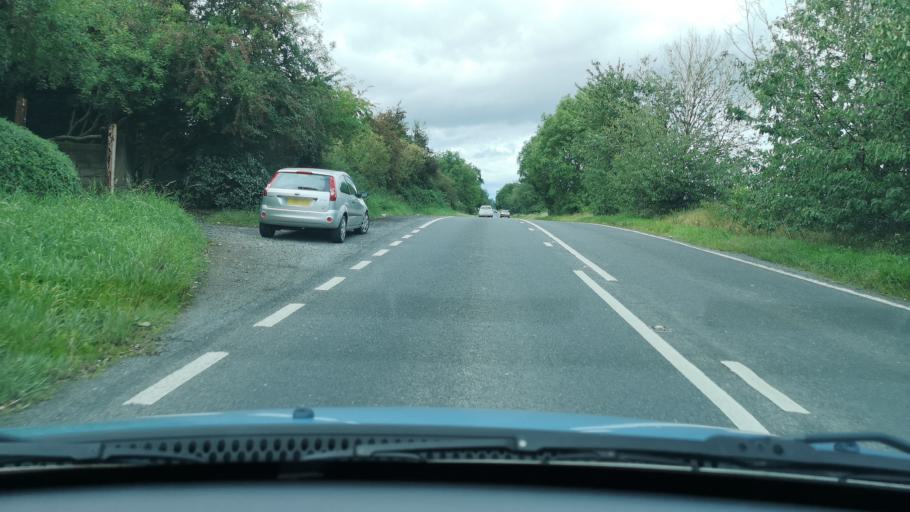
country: GB
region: England
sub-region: City and Borough of Wakefield
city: Low Ackworth
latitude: 53.6309
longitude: -1.3208
